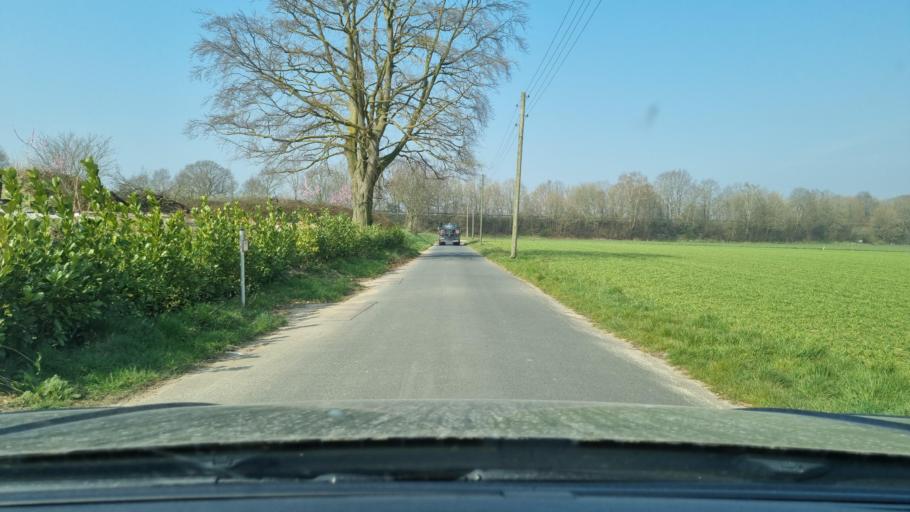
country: DE
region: North Rhine-Westphalia
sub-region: Regierungsbezirk Dusseldorf
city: Kranenburg
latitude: 51.7781
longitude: 6.0325
